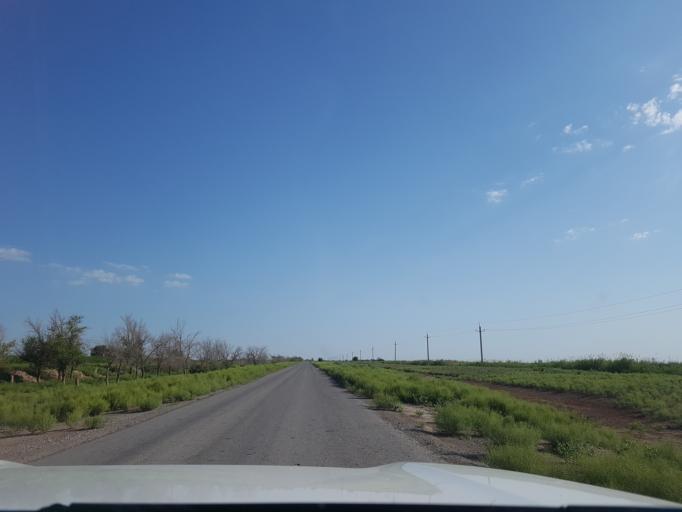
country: TM
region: Dasoguz
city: Koeneuergench
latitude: 41.8894
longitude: 58.7069
